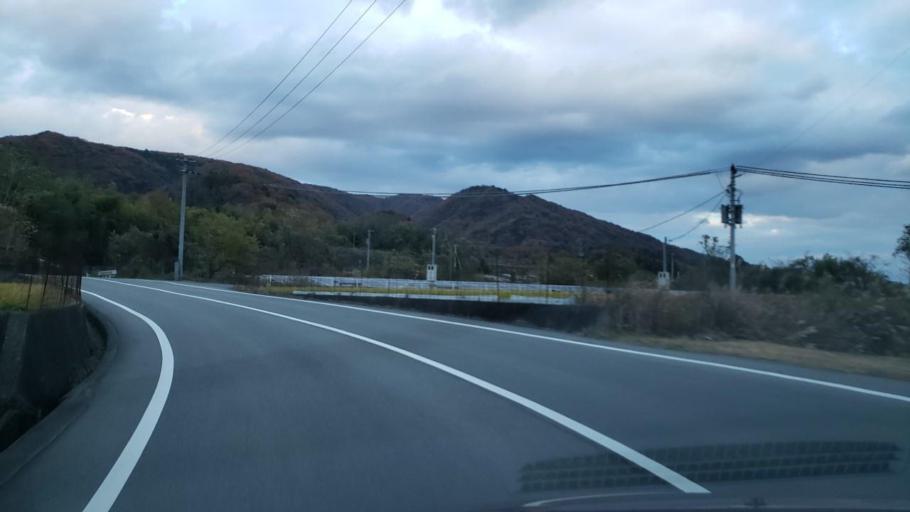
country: JP
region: Tokushima
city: Wakimachi
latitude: 34.0850
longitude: 134.1805
